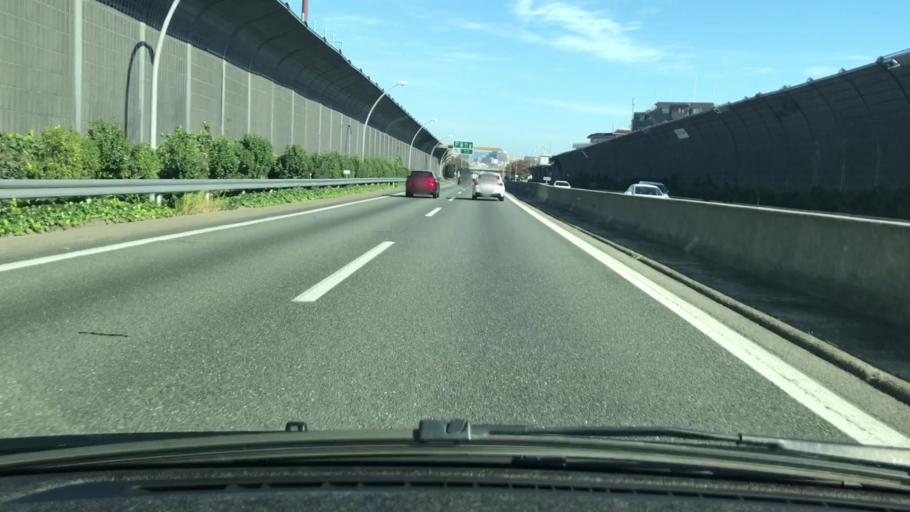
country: JP
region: Osaka
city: Suita
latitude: 34.7789
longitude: 135.5229
